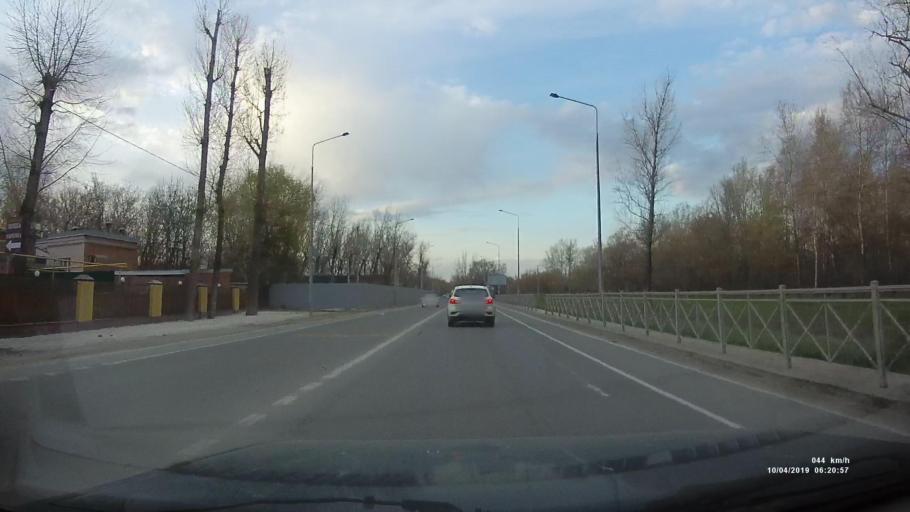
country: RU
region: Rostov
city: Bataysk
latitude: 47.2005
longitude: 39.7892
